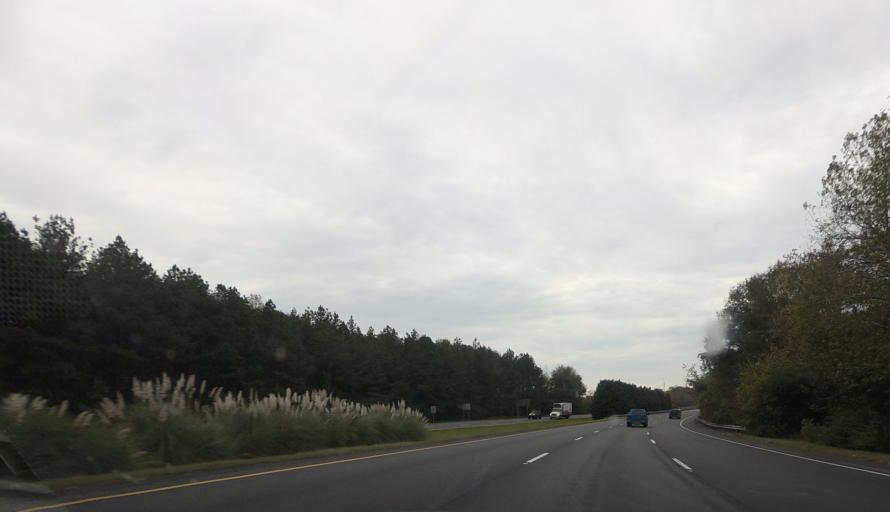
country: US
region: Alabama
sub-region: Russell County
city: Phenix City
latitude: 32.5091
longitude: -84.9938
